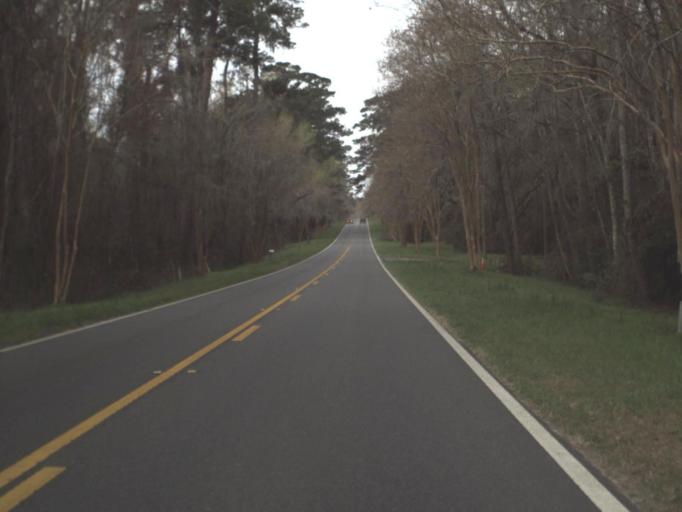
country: US
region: Florida
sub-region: Jefferson County
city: Monticello
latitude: 30.5288
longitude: -83.9850
